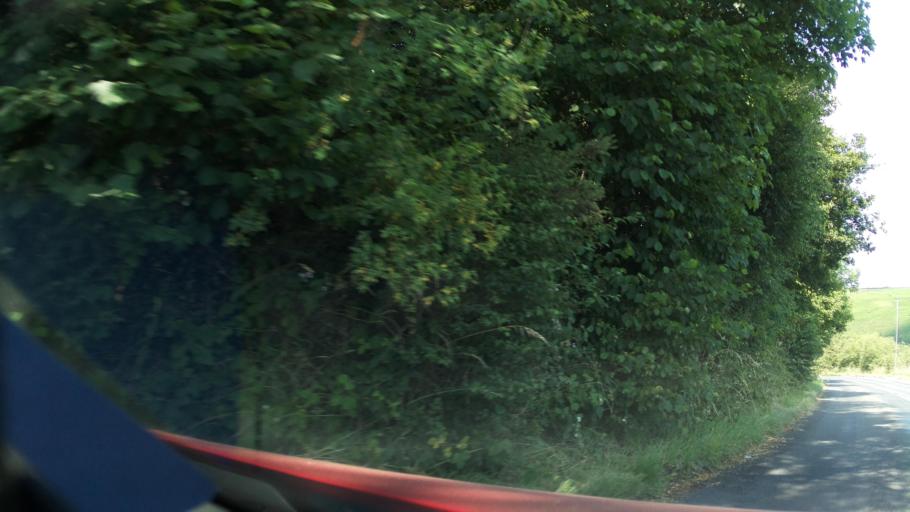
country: GB
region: Wales
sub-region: Caerphilly County Borough
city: Bargoed
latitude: 51.7023
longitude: -3.2274
